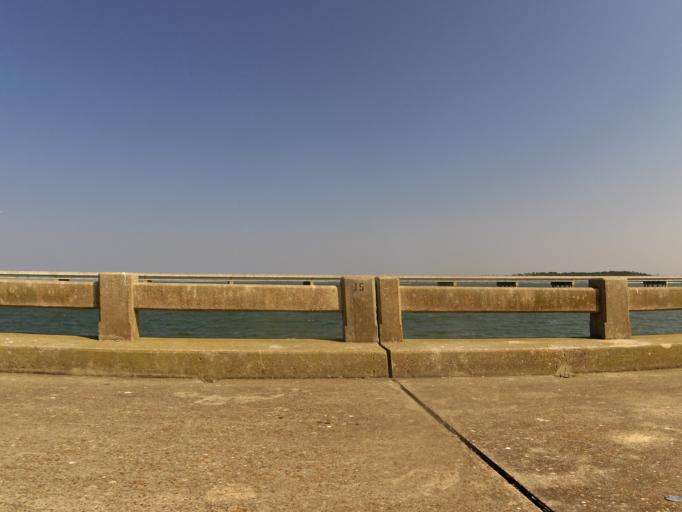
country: US
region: Florida
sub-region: Nassau County
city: Fernandina Beach
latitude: 30.5181
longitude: -81.4530
